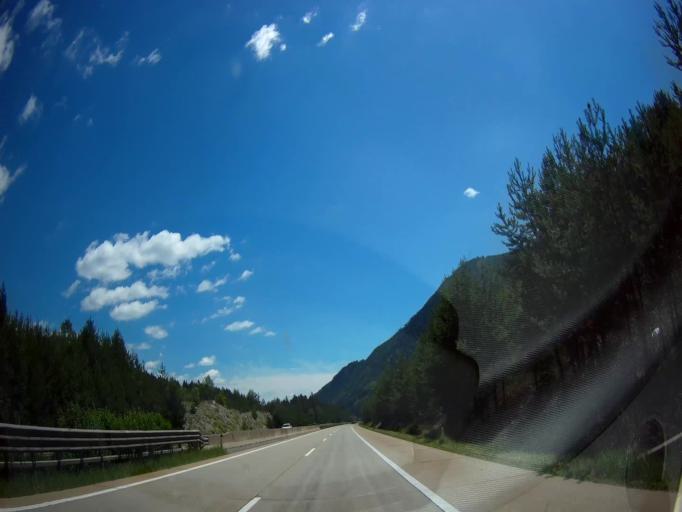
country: AT
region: Carinthia
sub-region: Politischer Bezirk Villach Land
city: Fresach
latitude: 46.6586
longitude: 13.7295
